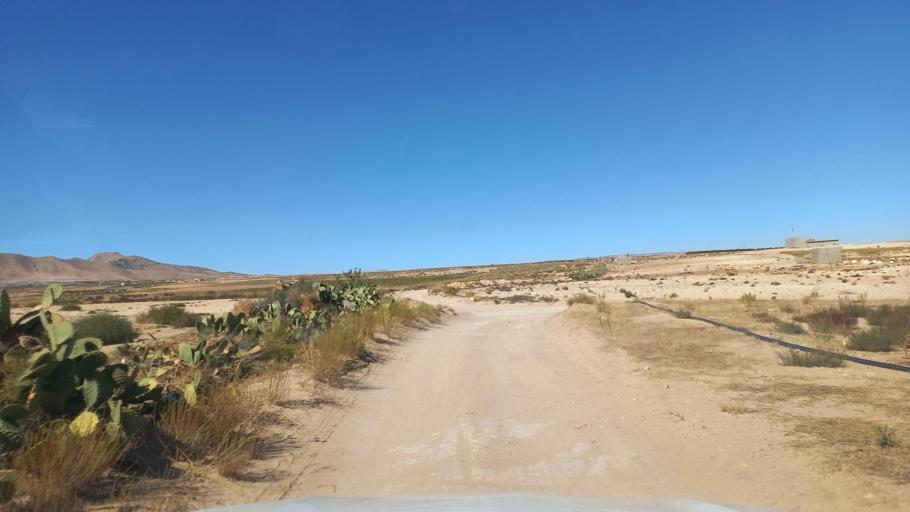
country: TN
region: Al Qasrayn
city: Sbiba
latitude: 35.4059
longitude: 9.0888
